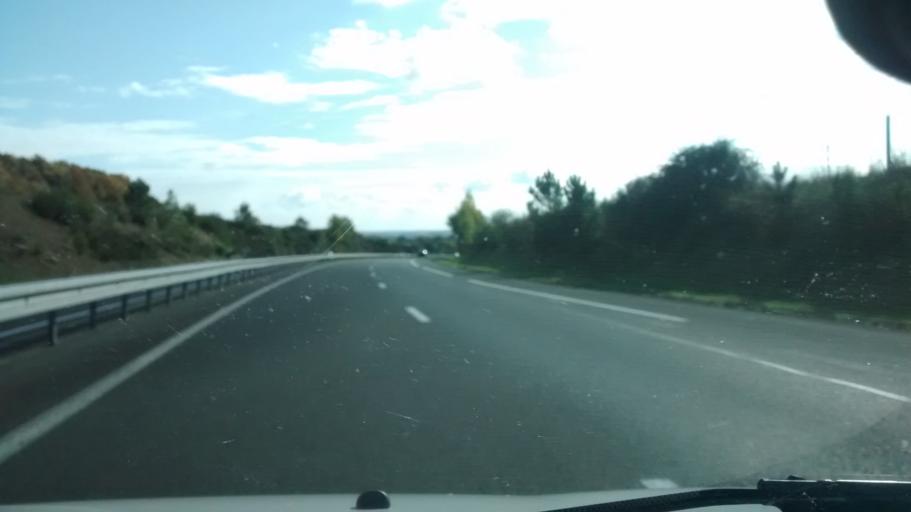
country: FR
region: Pays de la Loire
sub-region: Departement de Maine-et-Loire
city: Combree
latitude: 47.7133
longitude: -1.0065
